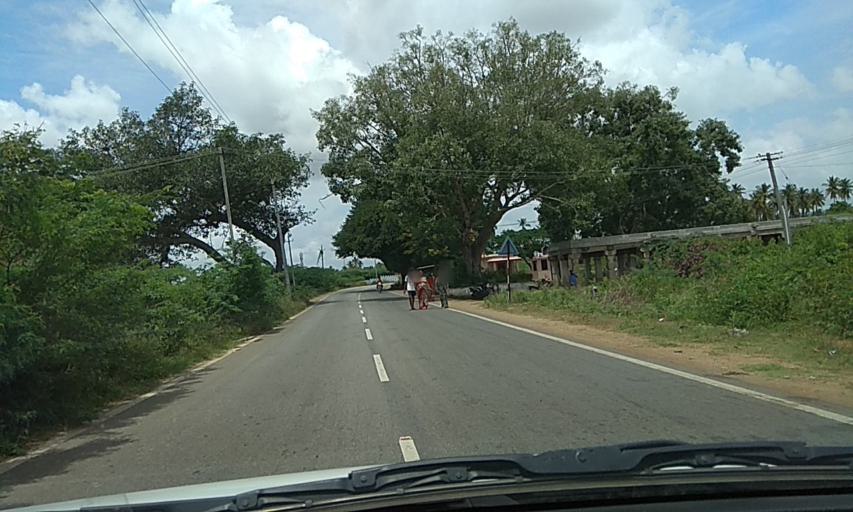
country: IN
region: Karnataka
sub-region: Chamrajnagar
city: Gundlupet
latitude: 11.8098
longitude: 76.7031
